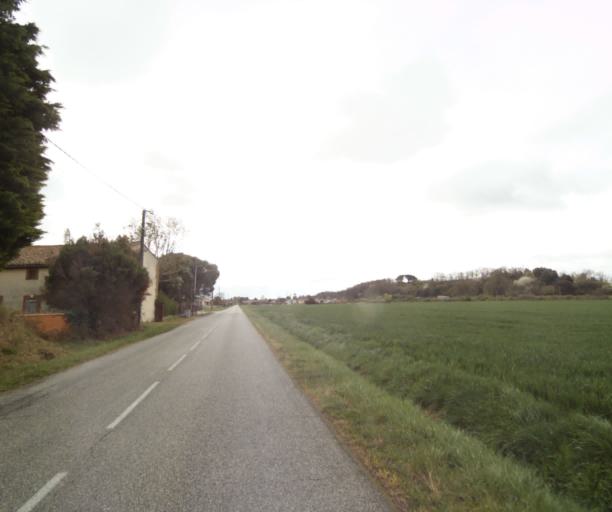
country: FR
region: Midi-Pyrenees
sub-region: Departement de l'Ariege
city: Saverdun
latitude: 43.2456
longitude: 1.5610
